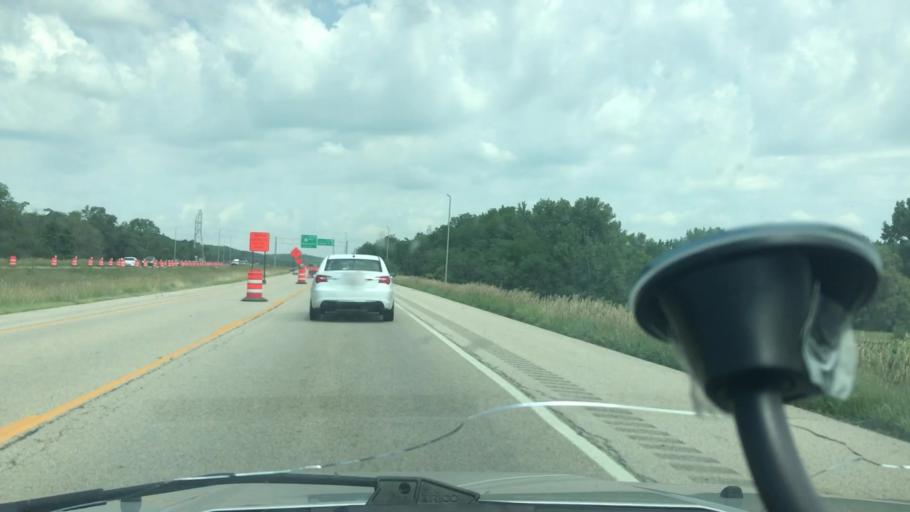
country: US
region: Illinois
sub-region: Peoria County
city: Bartonville
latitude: 40.6512
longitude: -89.6379
